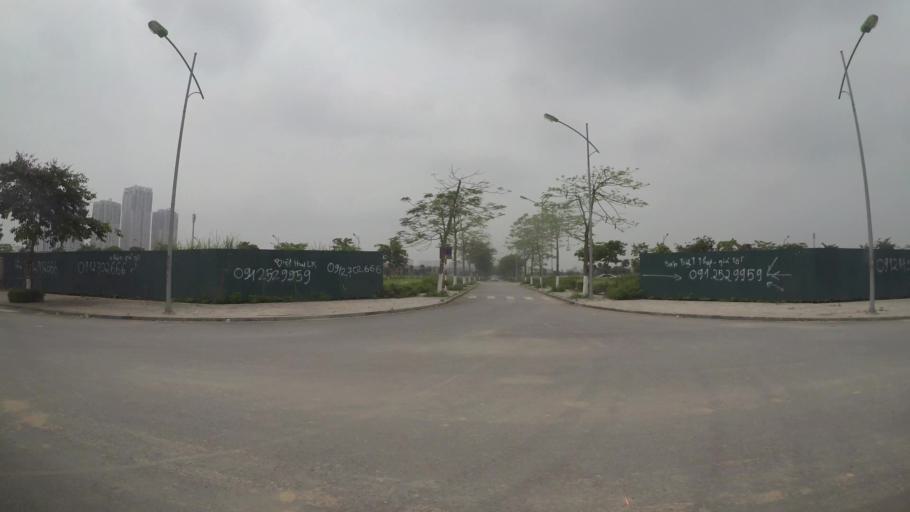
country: VN
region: Ha Noi
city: Ha Dong
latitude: 20.9803
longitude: 105.7557
